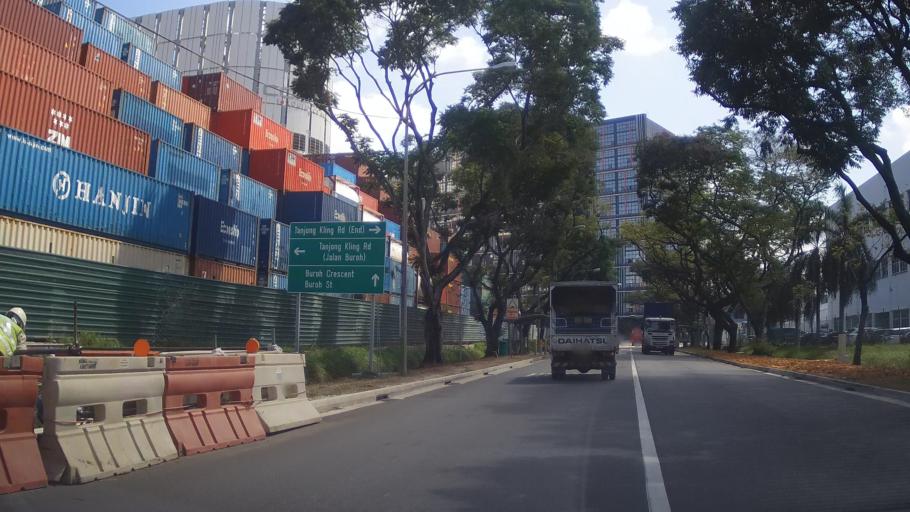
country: SG
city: Singapore
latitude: 1.3085
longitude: 103.6961
